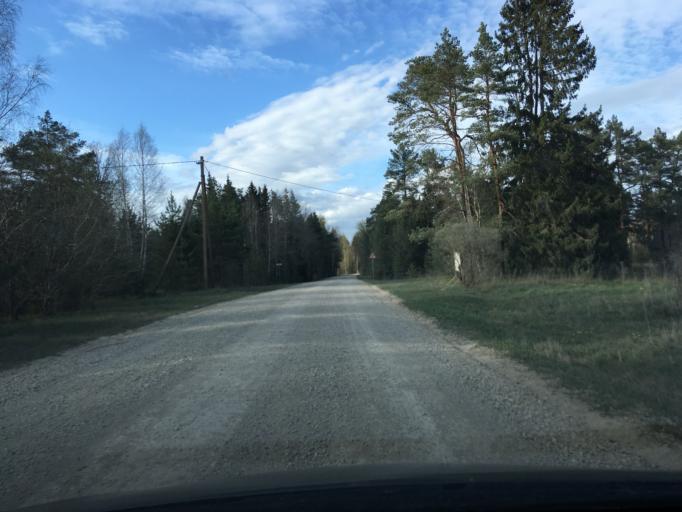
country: EE
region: Raplamaa
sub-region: Maerjamaa vald
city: Marjamaa
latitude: 58.9668
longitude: 24.3315
